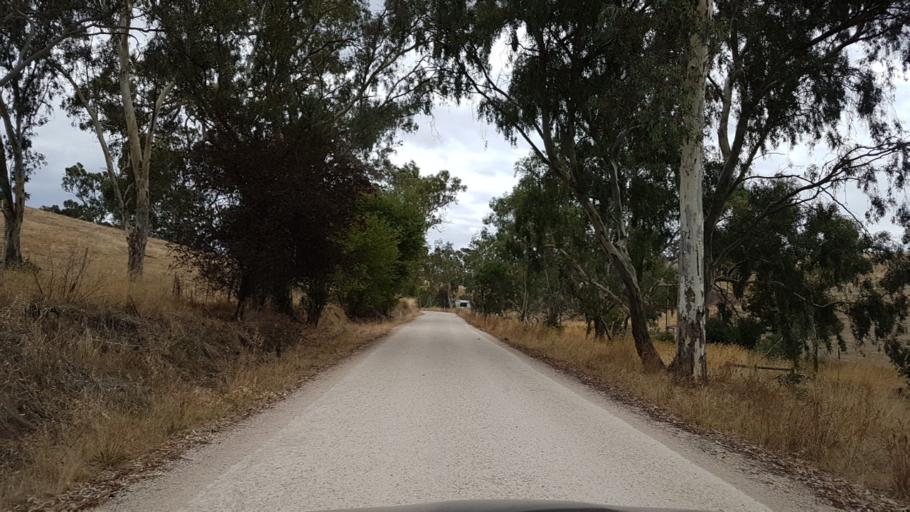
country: AU
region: South Australia
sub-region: Adelaide Hills
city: Gumeracha
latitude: -34.8081
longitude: 138.8103
